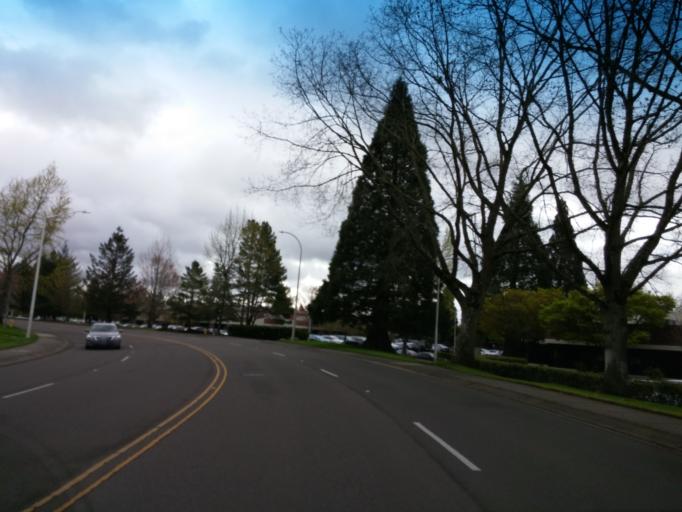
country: US
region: Oregon
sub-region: Washington County
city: Cedar Mill
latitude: 45.5250
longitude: -122.8302
